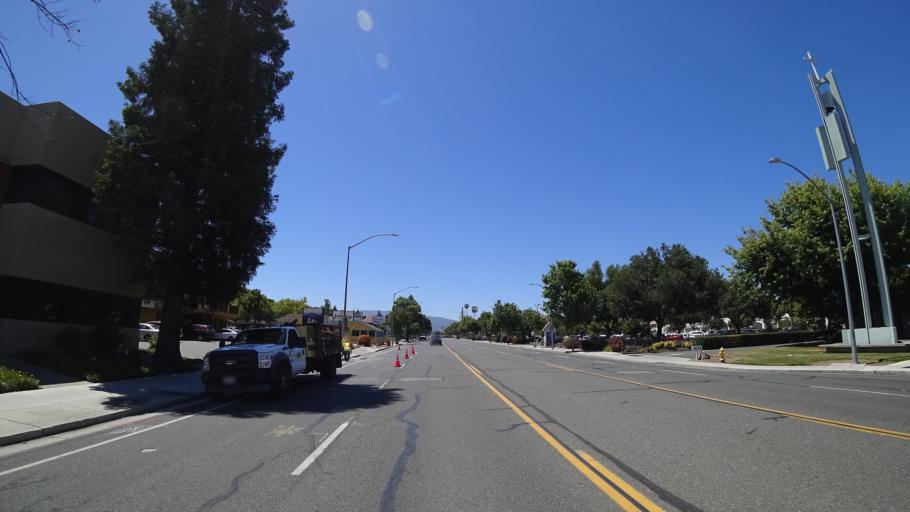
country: US
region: California
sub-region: Santa Clara County
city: Campbell
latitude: 37.2927
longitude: -121.9499
